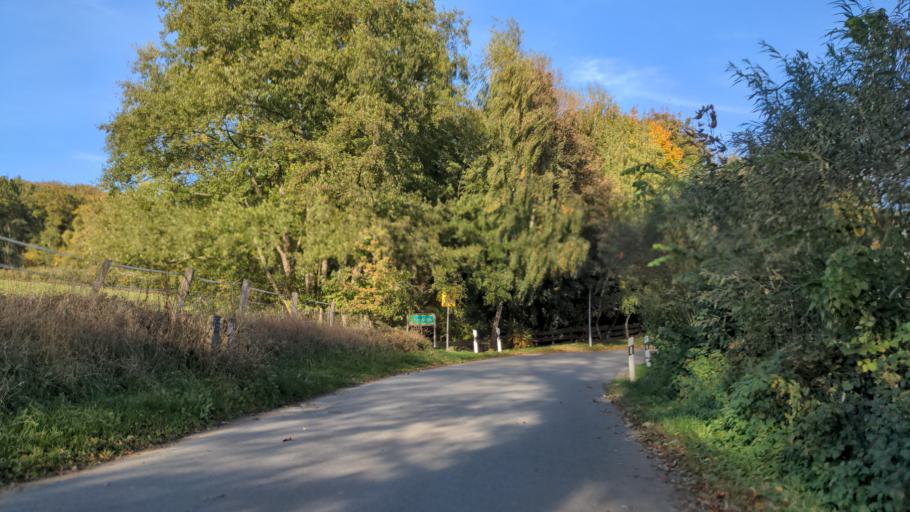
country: DE
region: Schleswig-Holstein
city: Kirchnuchel
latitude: 54.1903
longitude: 10.6757
